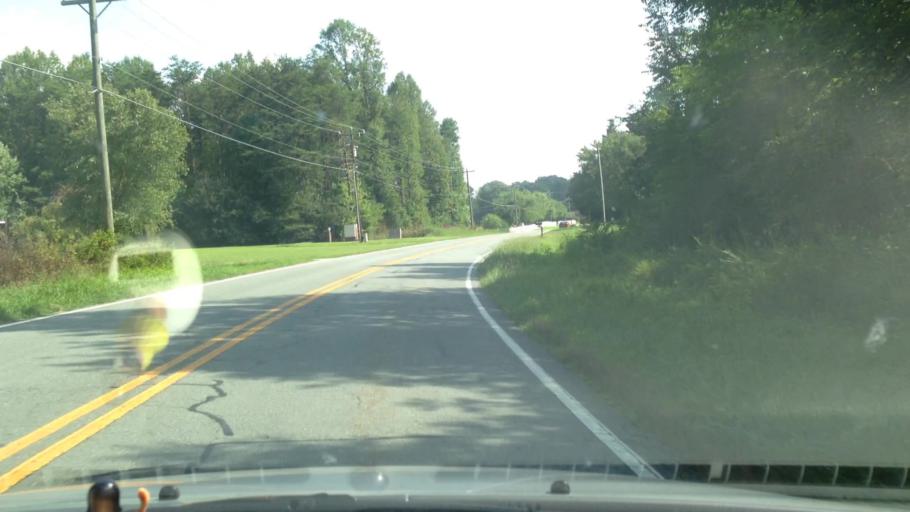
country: US
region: North Carolina
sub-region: Guilford County
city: Oak Ridge
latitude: 36.2114
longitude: -80.0553
